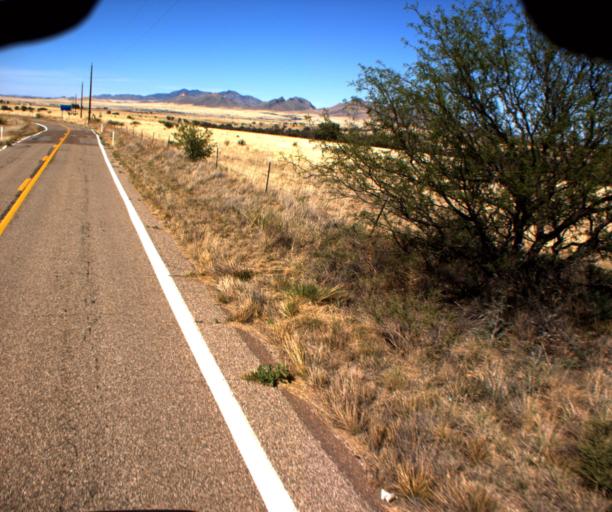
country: US
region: Arizona
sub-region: Cochise County
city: Huachuca City
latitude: 31.5973
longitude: -110.5583
